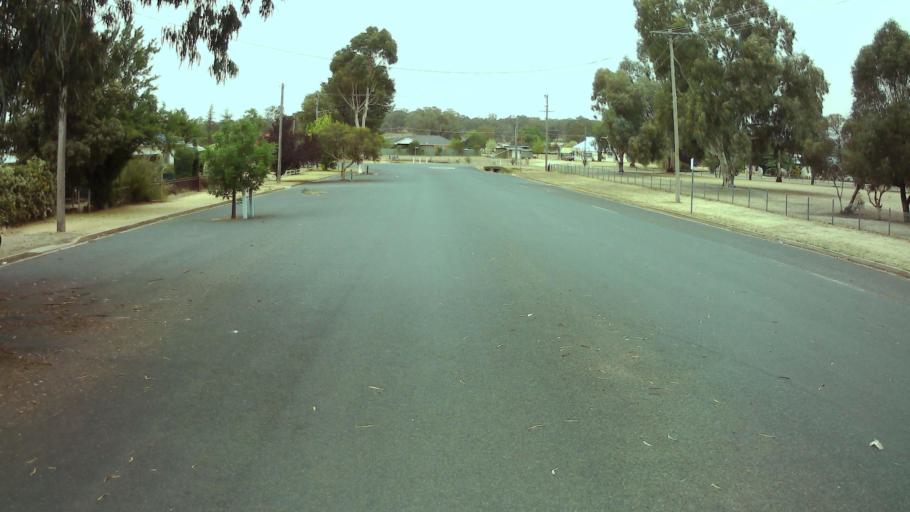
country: AU
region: New South Wales
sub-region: Weddin
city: Grenfell
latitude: -33.8923
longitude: 148.1662
